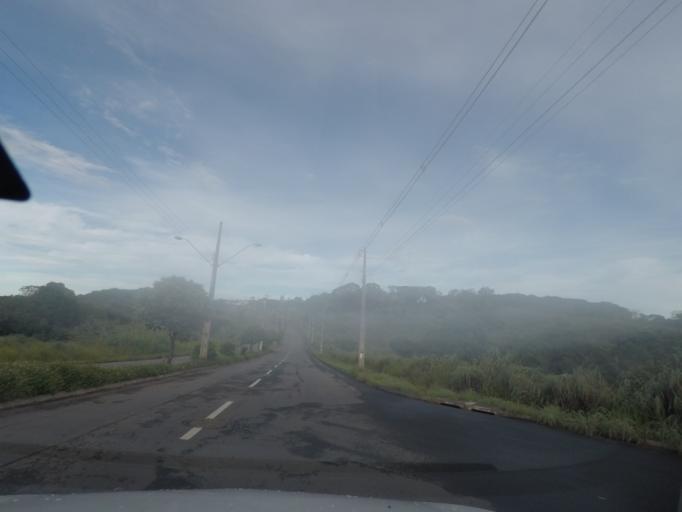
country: BR
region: Goias
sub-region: Aparecida De Goiania
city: Aparecida de Goiania
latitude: -16.7846
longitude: -49.3760
